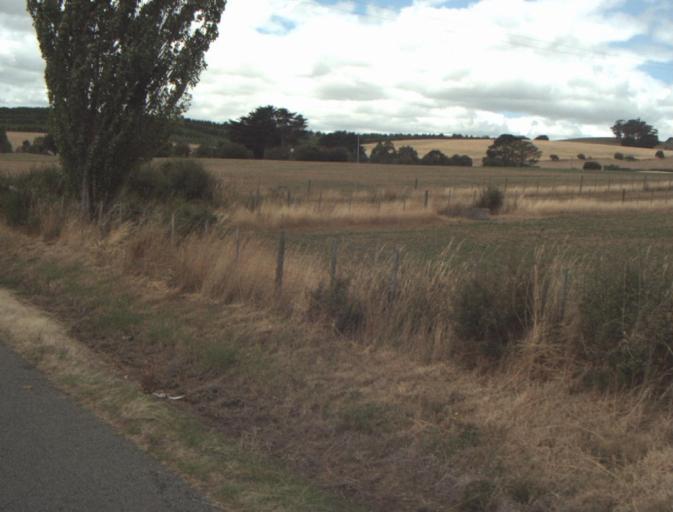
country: AU
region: Tasmania
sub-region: Northern Midlands
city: Evandale
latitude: -41.5165
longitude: 147.2530
